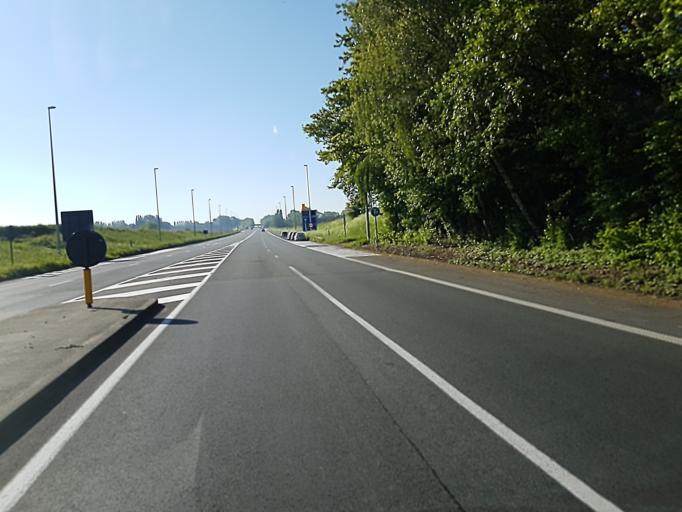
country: BE
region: Wallonia
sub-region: Province du Hainaut
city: Mouscron
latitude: 50.7691
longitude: 3.1915
